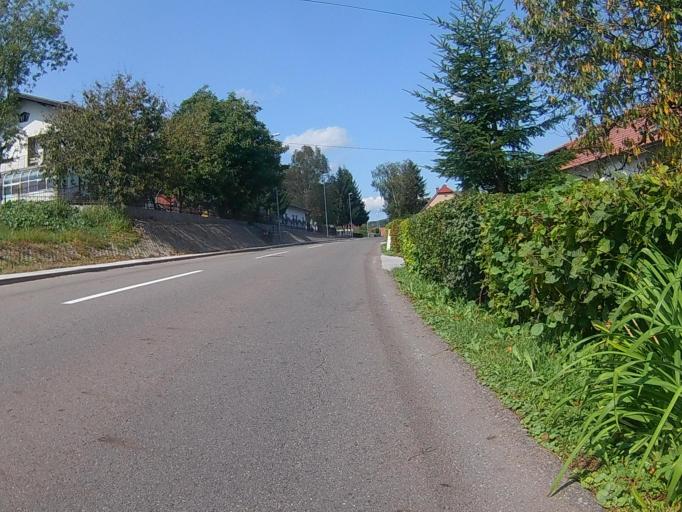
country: SI
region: Ptuj
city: Ptuj
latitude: 46.4321
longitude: 15.8586
